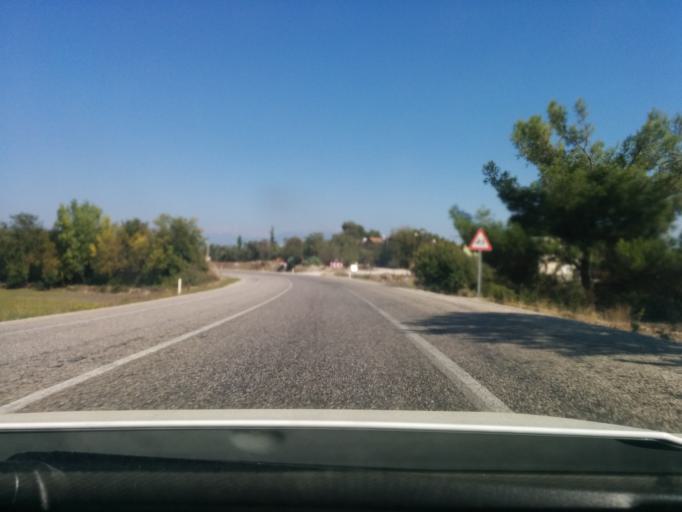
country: TR
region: Mugla
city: Kemer
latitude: 36.5601
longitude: 29.3481
